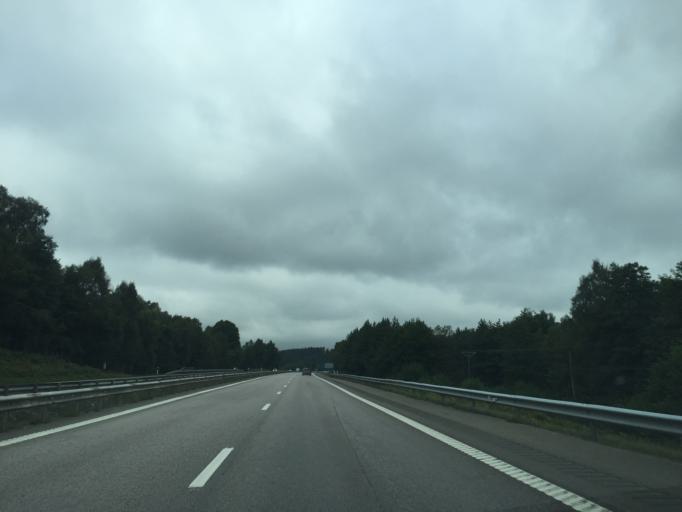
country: SE
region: Halland
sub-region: Kungsbacka Kommun
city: Frillesas
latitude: 57.3784
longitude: 12.1968
